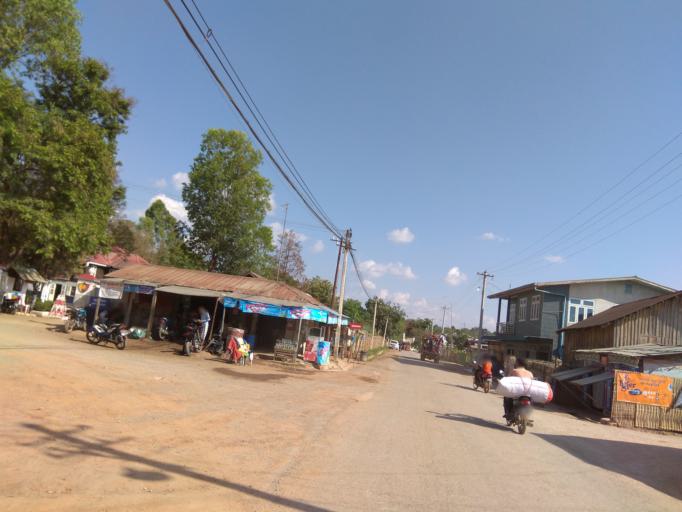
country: MM
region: Shan
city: Taunggyi
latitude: 20.6582
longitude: 96.6370
